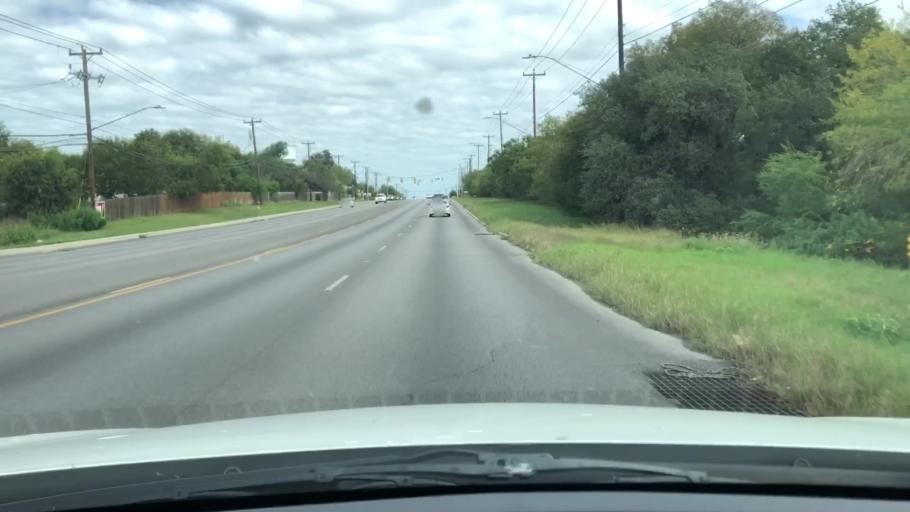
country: US
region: Texas
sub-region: Bexar County
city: Leon Valley
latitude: 29.4773
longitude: -98.6480
